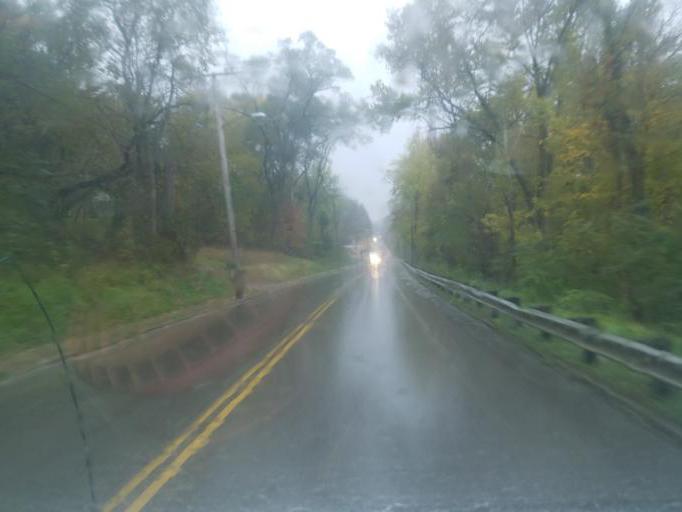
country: US
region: Ohio
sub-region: Muskingum County
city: Zanesville
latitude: 39.9282
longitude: -82.0018
